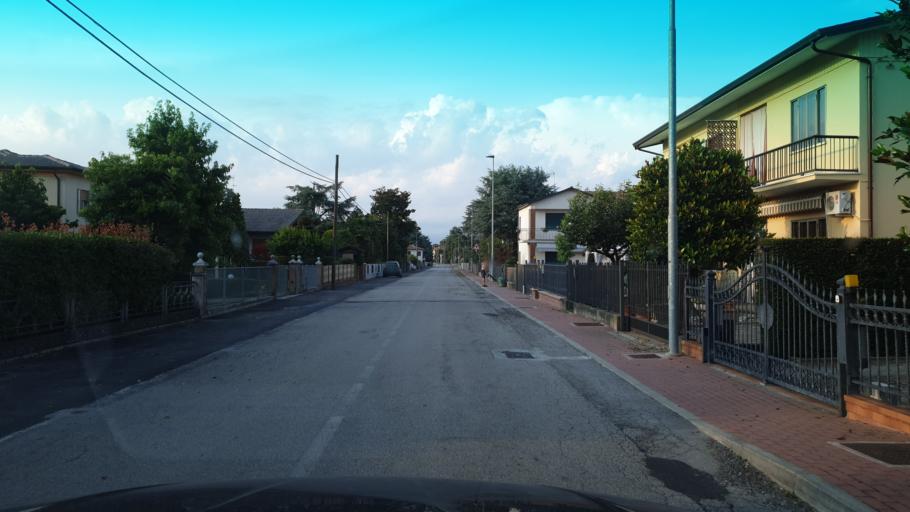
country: IT
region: Veneto
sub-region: Provincia di Rovigo
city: Castelguglielmo
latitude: 45.0196
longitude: 11.5352
